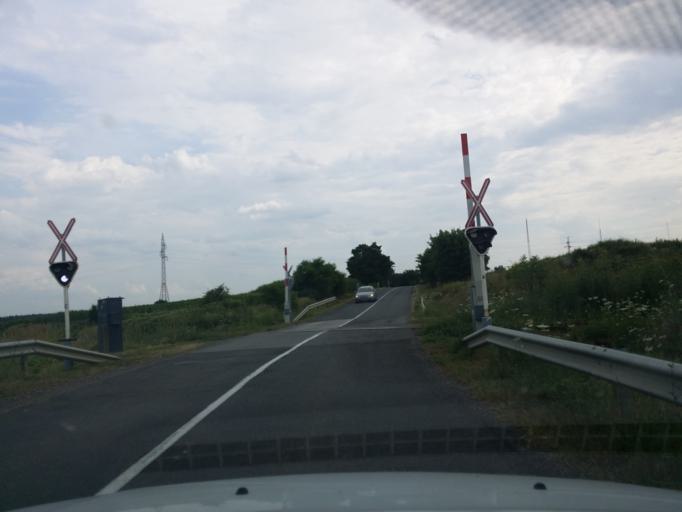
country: HU
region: Nograd
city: Bercel
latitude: 47.8919
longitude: 19.3695
